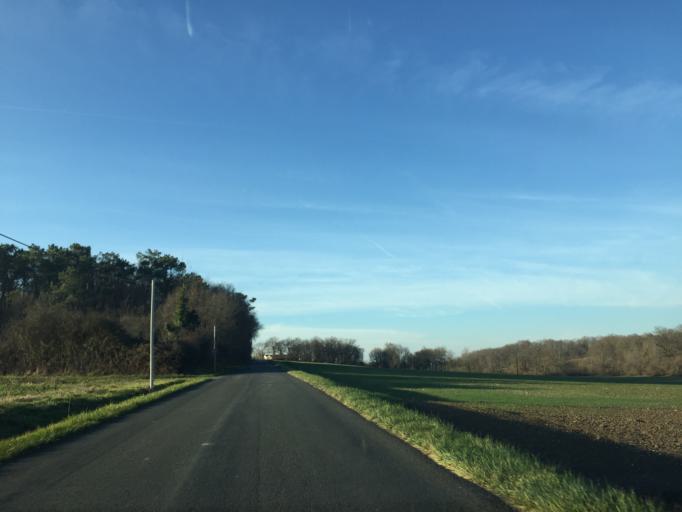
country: FR
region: Aquitaine
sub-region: Departement de la Dordogne
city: Saint-Aulaye
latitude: 45.2505
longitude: 0.2131
